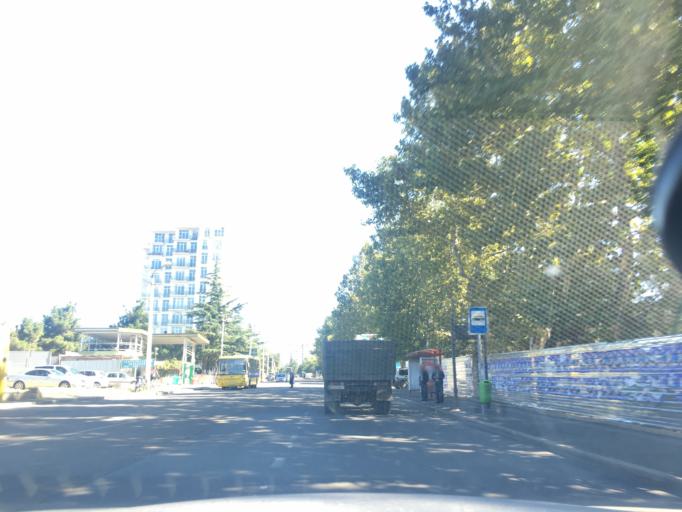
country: GE
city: Zahesi
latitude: 41.7883
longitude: 44.8015
